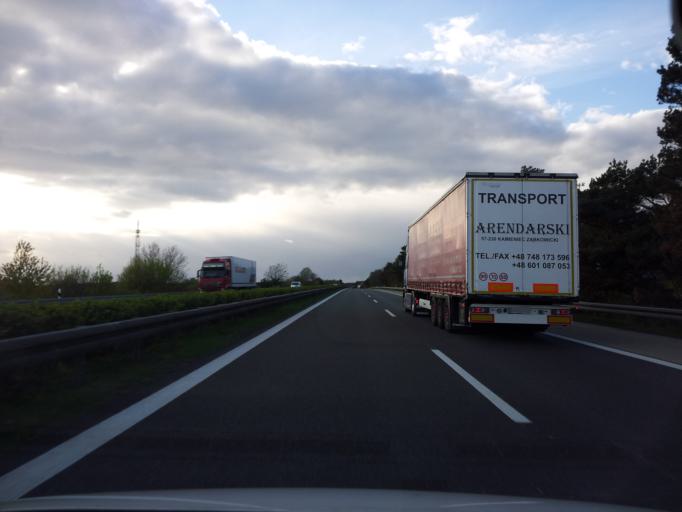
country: DE
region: Brandenburg
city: Vetschau
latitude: 51.8111
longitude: 14.0282
